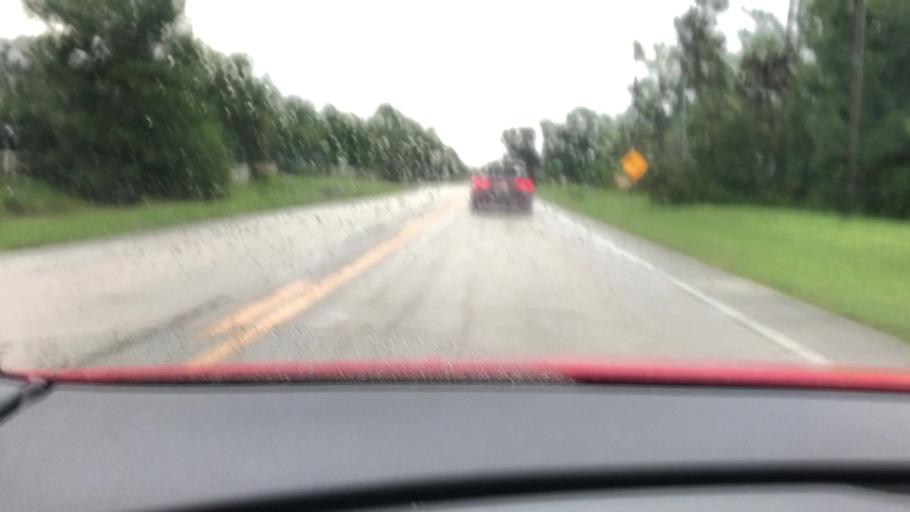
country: US
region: Florida
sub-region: Volusia County
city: Samsula-Spruce Creek
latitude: 29.0708
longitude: -81.0681
